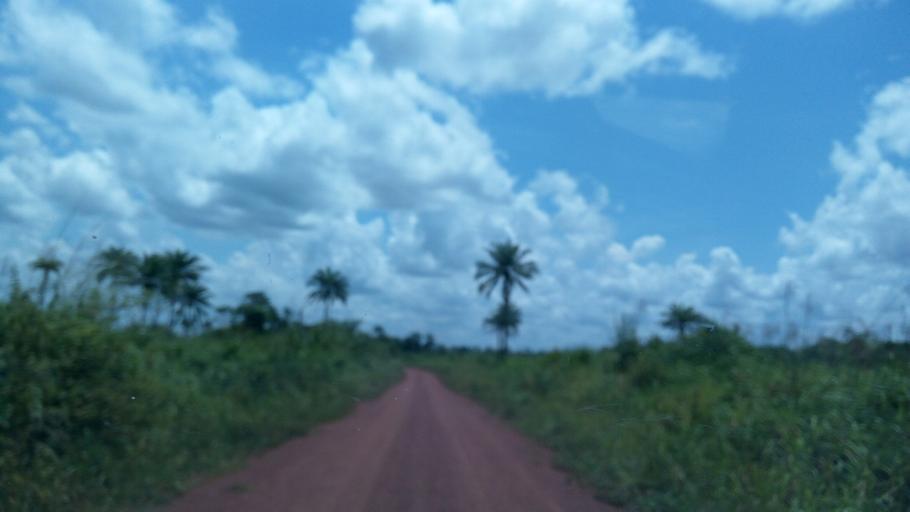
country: CD
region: Equateur
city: Libenge
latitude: 3.7548
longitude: 18.8125
